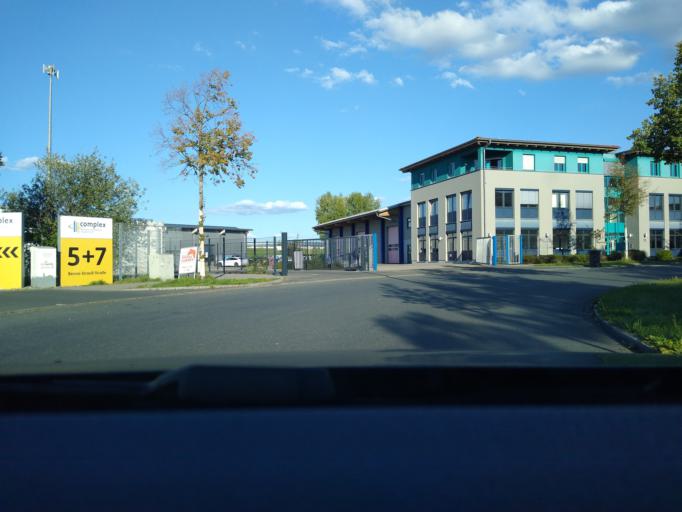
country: DE
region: Bavaria
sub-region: Regierungsbezirk Mittelfranken
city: Furth
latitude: 49.4491
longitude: 10.9914
